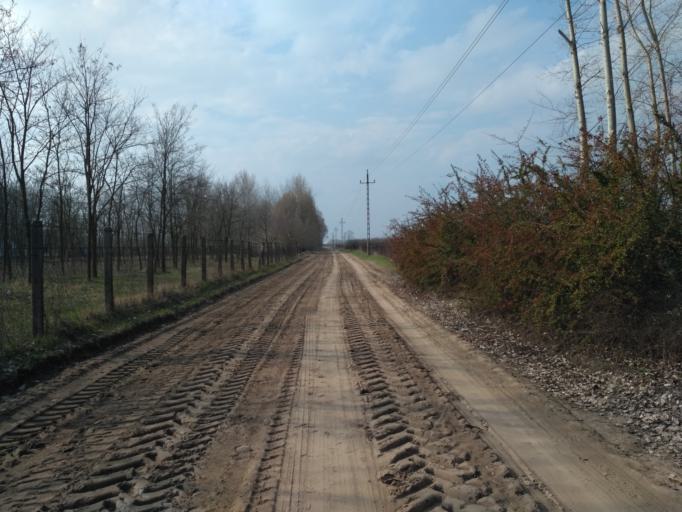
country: HU
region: Bacs-Kiskun
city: Tiszakecske
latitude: 46.9467
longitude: 20.0807
